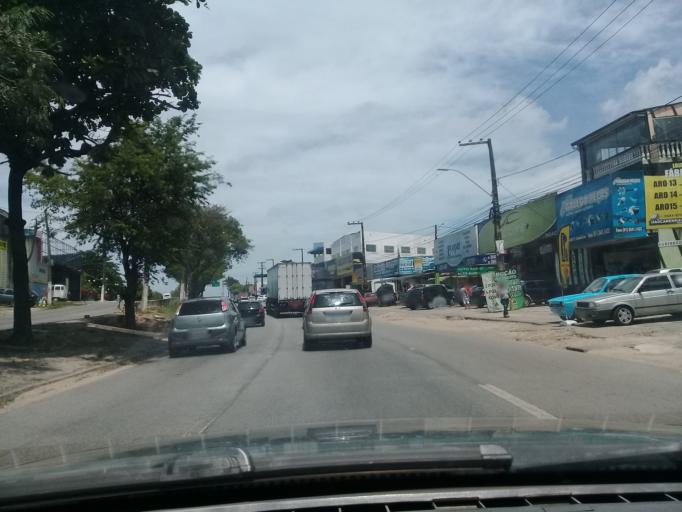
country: BR
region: Pernambuco
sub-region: Abreu E Lima
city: Abreu e Lima
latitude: -7.9102
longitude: -34.9020
